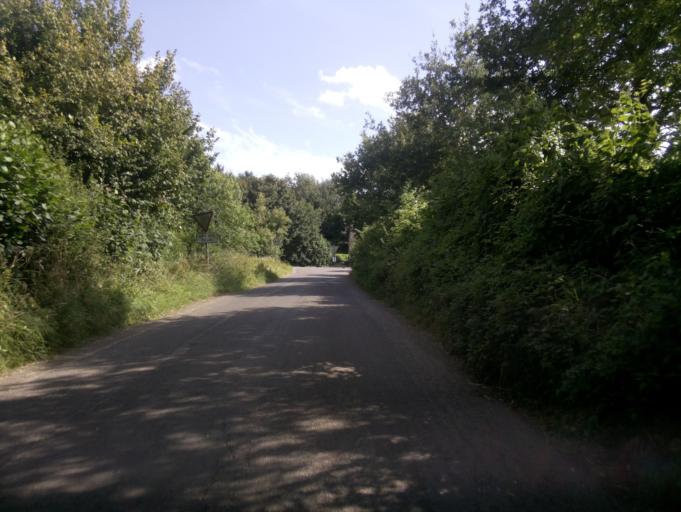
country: GB
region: England
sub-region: Gloucestershire
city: Tetbury
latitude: 51.6484
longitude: -2.1439
